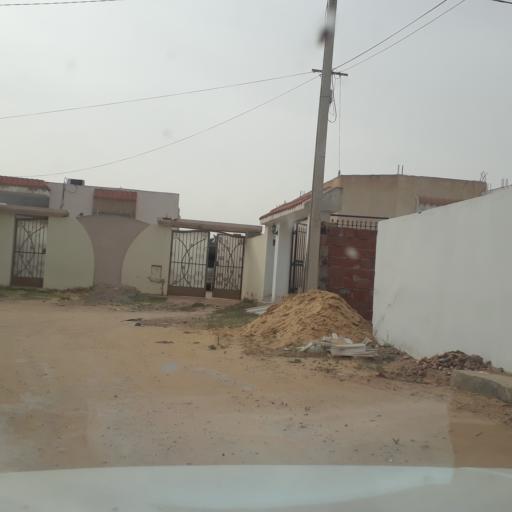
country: TN
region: Safaqis
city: Al Qarmadah
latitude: 34.8273
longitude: 10.7756
